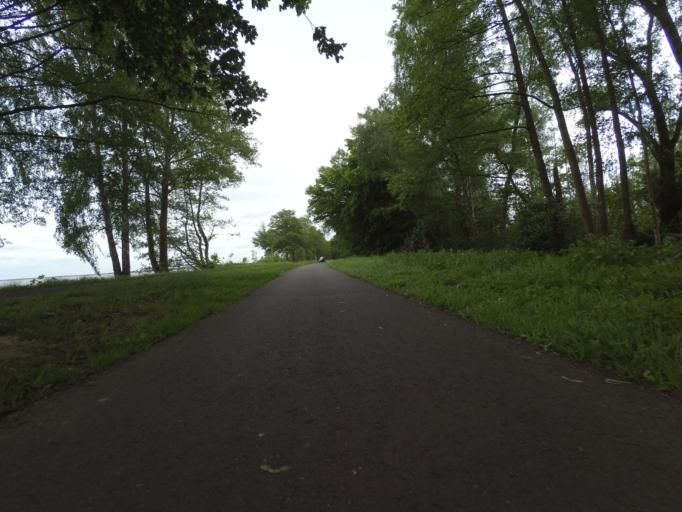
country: DE
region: Lower Saxony
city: Hagenburg
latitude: 52.4468
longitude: 9.3199
